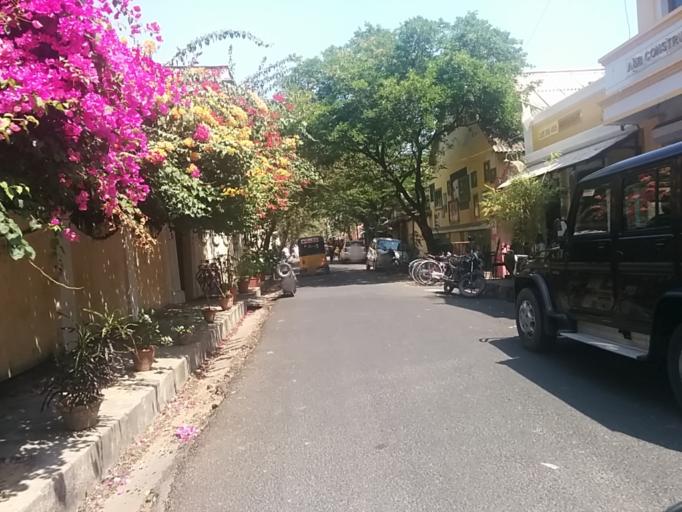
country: IN
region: Pondicherry
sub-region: Puducherry
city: Puducherry
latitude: 11.9294
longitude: 79.8339
